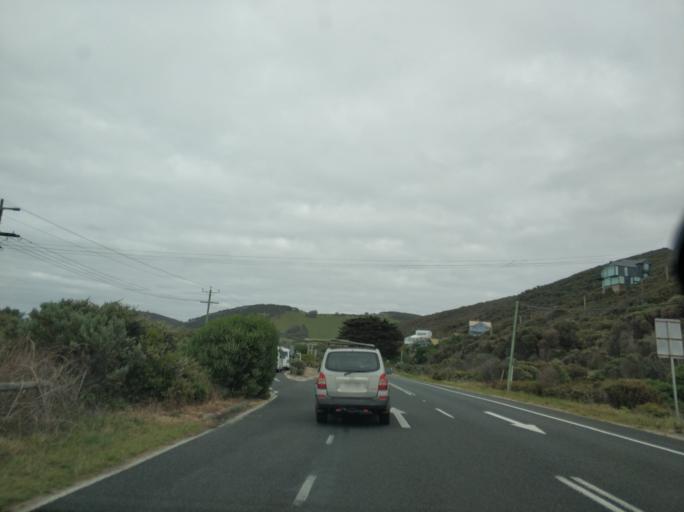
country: AU
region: Victoria
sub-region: Surf Coast
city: Anglesea
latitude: -38.4715
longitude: 144.0460
